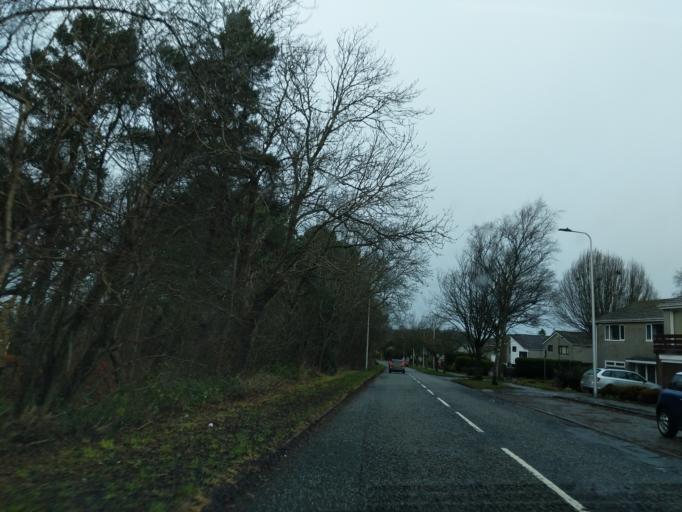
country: GB
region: Scotland
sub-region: Edinburgh
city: Balerno
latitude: 55.8764
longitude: -3.3475
